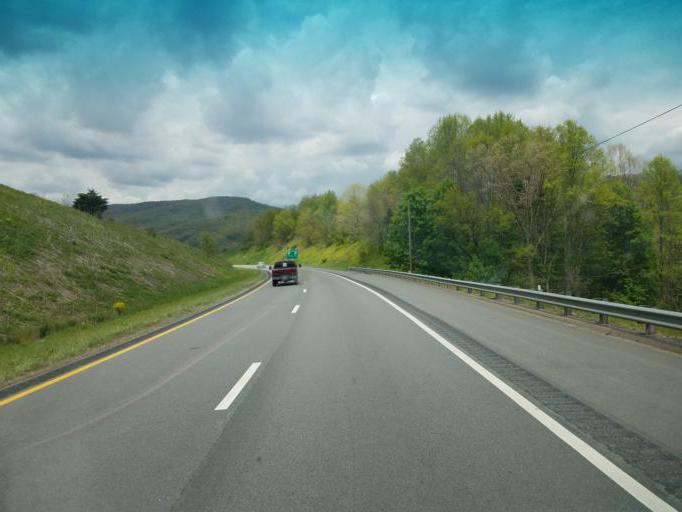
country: US
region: West Virginia
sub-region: Mercer County
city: Bluefield
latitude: 37.2366
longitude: -81.0977
